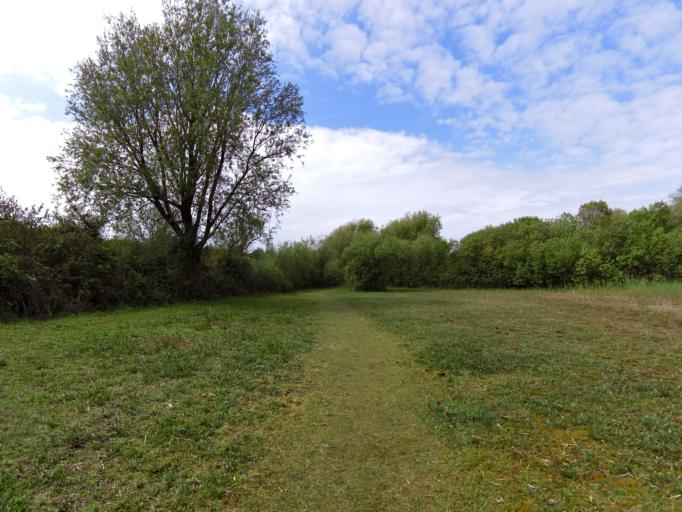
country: NL
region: Zeeland
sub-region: Schouwen-Duiveland
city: Scharendijke
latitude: 51.7825
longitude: 3.8744
